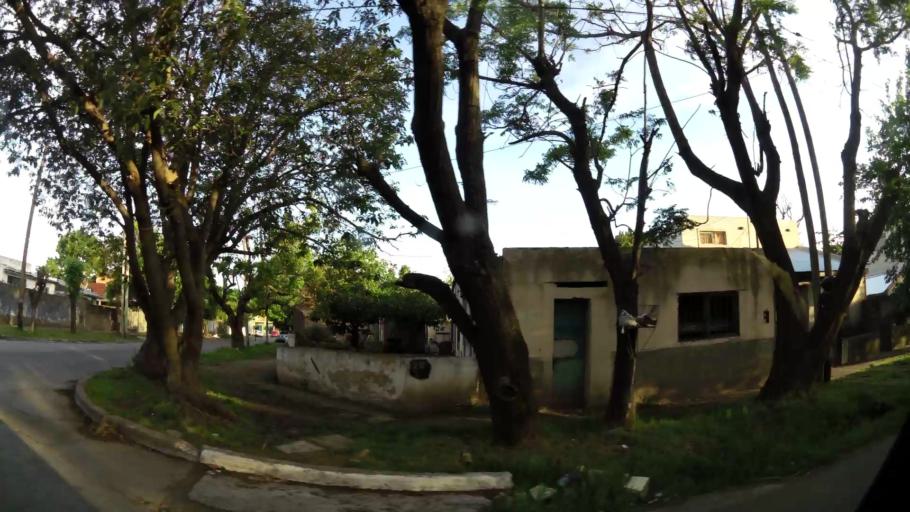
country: AR
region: Buenos Aires
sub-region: Partido de Quilmes
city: Quilmes
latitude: -34.7750
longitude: -58.1988
